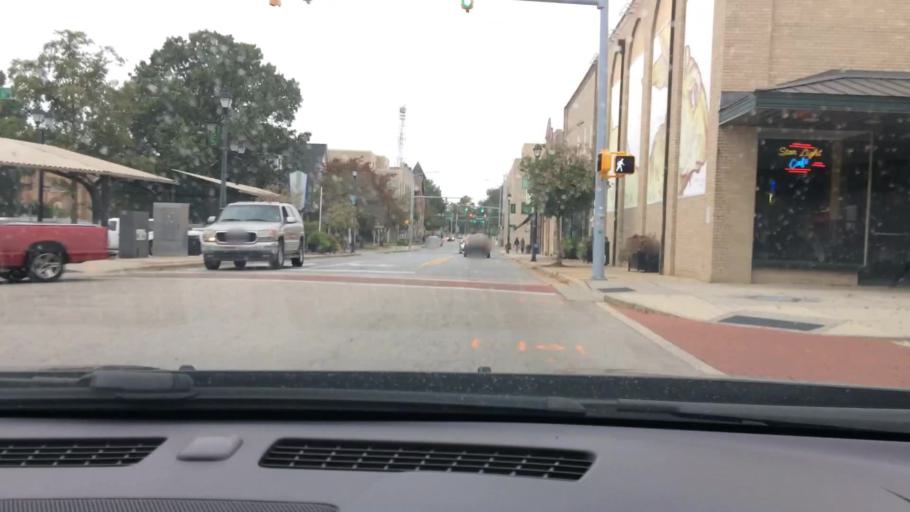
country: US
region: North Carolina
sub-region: Pitt County
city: Greenville
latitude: 35.6112
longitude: -77.3729
